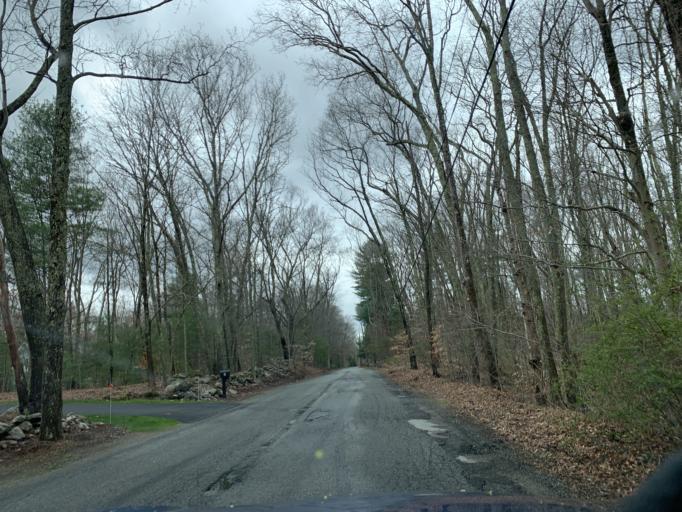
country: US
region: Massachusetts
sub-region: Bristol County
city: Rehoboth
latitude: 41.8875
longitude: -71.2077
